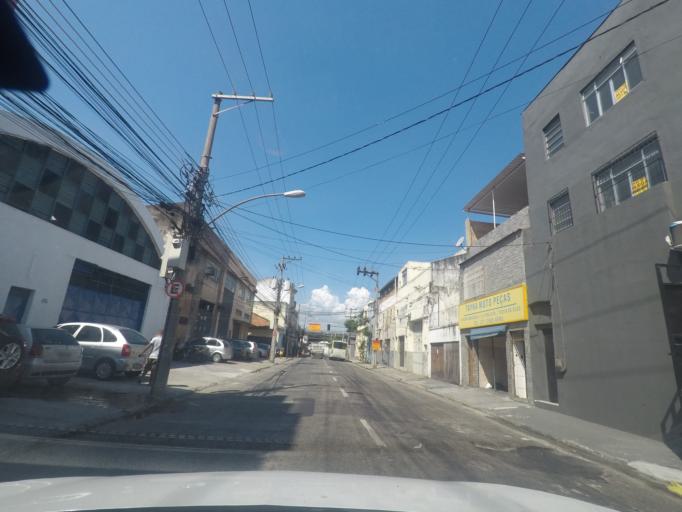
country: BR
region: Rio de Janeiro
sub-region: Rio De Janeiro
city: Rio de Janeiro
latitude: -22.8911
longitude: -43.2199
